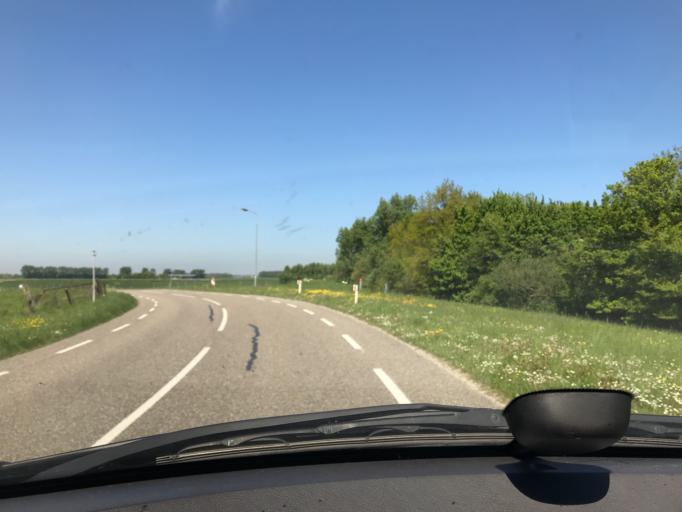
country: NL
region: Zeeland
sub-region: Gemeente Veere
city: Veere
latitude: 51.5101
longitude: 3.7011
